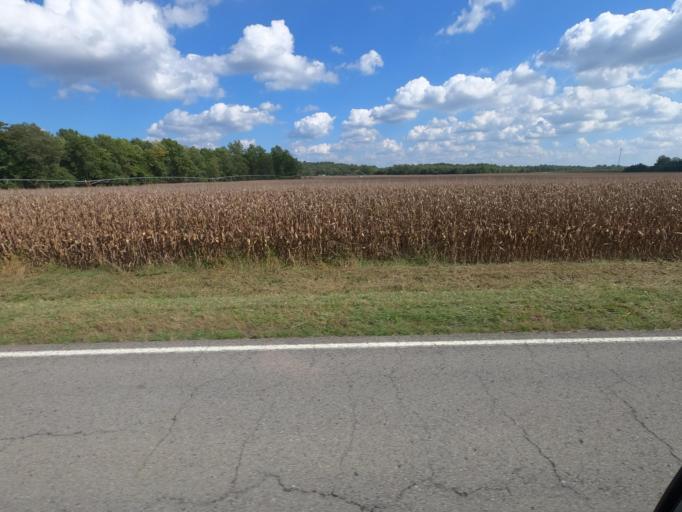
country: US
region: Illinois
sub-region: Massac County
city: Metropolis
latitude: 37.2887
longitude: -88.7569
